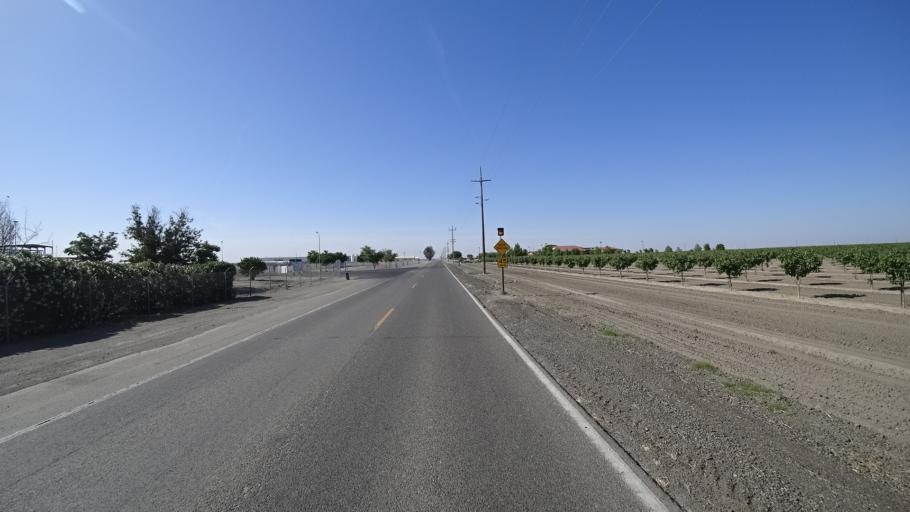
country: US
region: California
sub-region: Kings County
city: Corcoran
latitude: 36.0685
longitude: -119.5720
